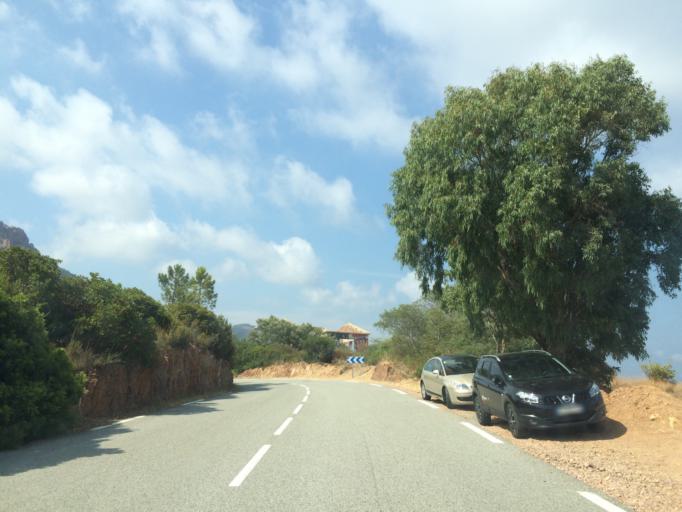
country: FR
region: Provence-Alpes-Cote d'Azur
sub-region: Departement des Alpes-Maritimes
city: Theoule-sur-Mer
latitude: 43.4557
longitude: 6.9214
